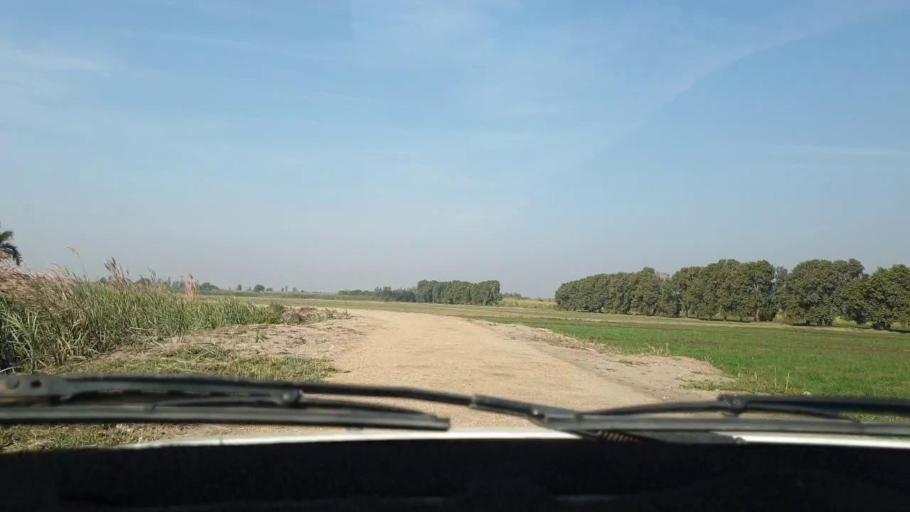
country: PK
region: Sindh
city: Tando Muhammad Khan
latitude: 25.0011
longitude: 68.4591
